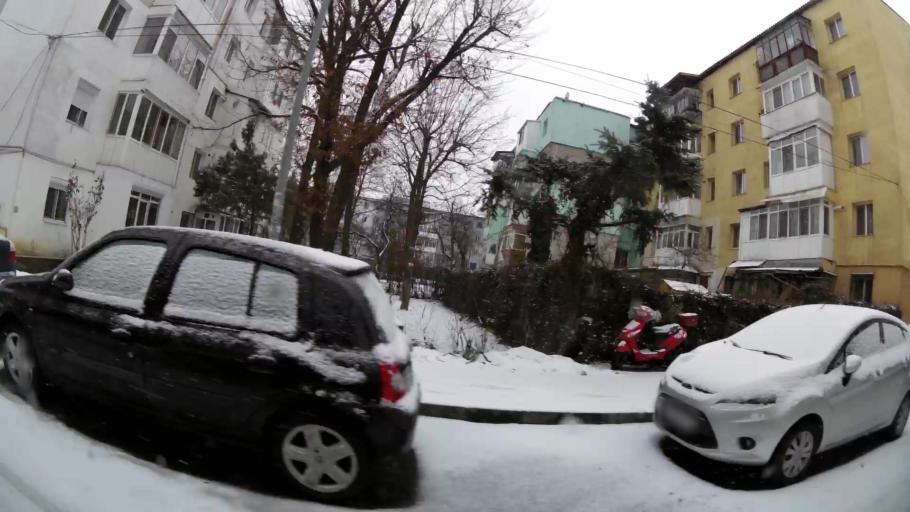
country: RO
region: Dambovita
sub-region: Municipiul Targoviste
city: Targoviste
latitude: 44.9250
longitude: 25.4426
